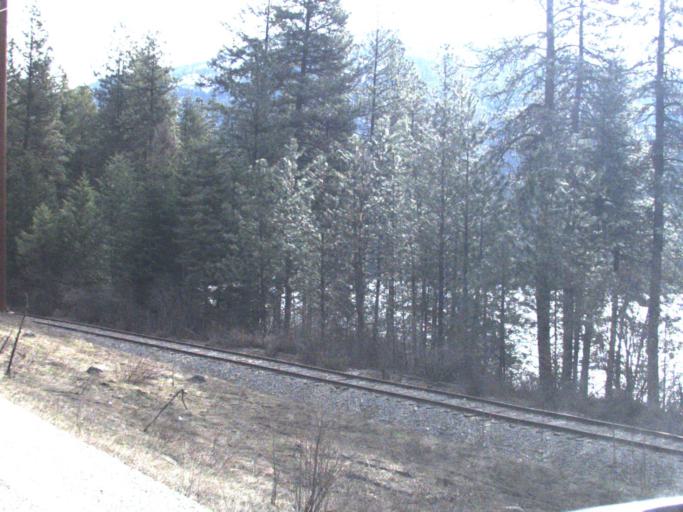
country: US
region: Washington
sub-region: Pend Oreille County
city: Newport
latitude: 48.4785
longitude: -117.2771
